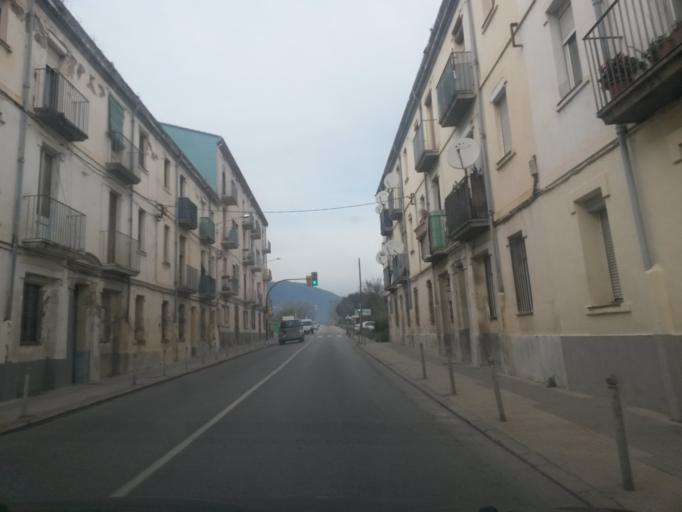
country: ES
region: Catalonia
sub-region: Provincia de Girona
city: Angles
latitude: 41.9602
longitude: 2.6327
